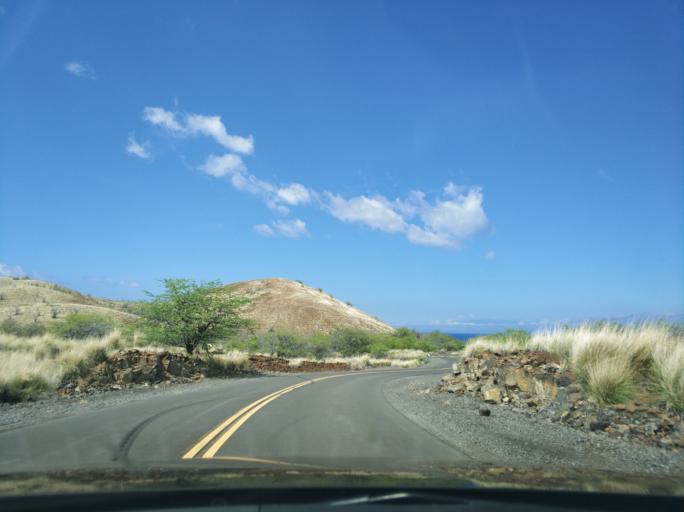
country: US
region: Hawaii
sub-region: Hawaii County
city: Kalaoa
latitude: 19.7972
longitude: -156.0070
